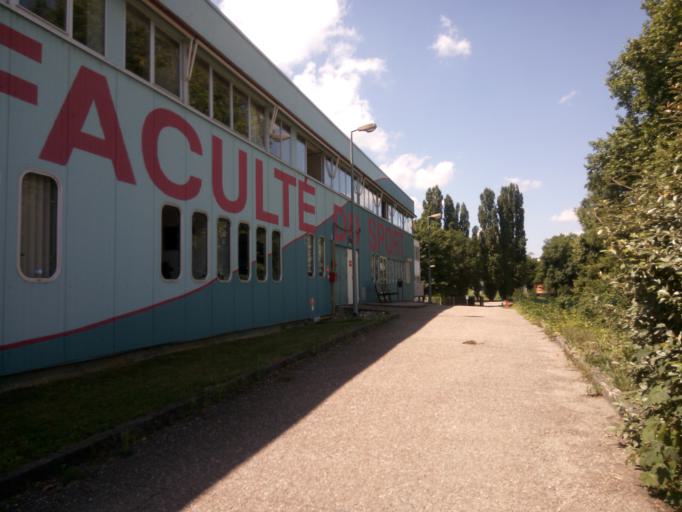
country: FR
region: Lorraine
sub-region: Departement de Meurthe-et-Moselle
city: Villers-les-Nancy
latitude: 48.6663
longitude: 6.1563
